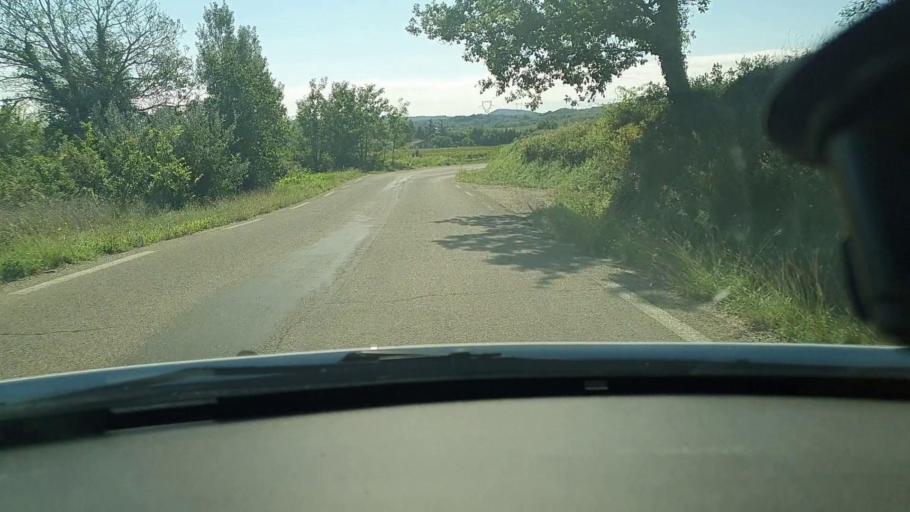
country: FR
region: Languedoc-Roussillon
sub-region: Departement du Gard
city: Saint-Julien-de-Peyrolas
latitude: 44.2710
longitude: 4.5715
